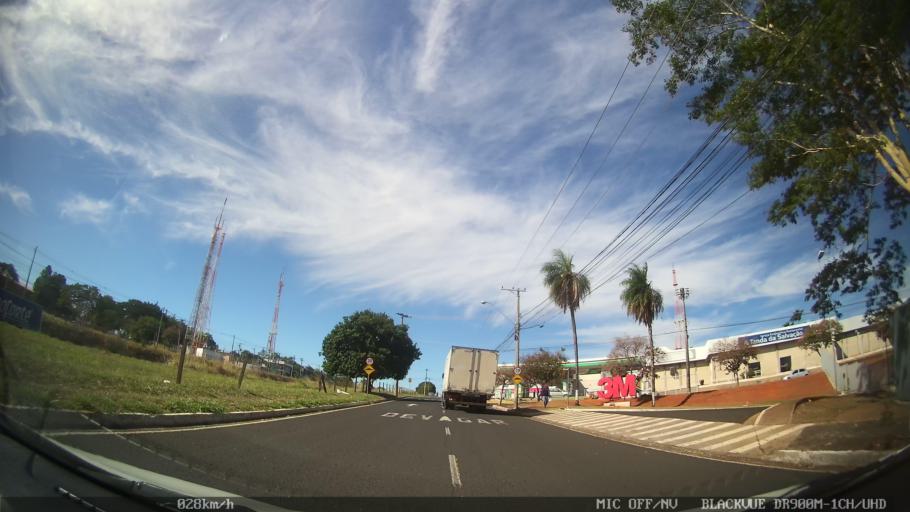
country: BR
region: Sao Paulo
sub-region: Sao Jose Do Rio Preto
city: Sao Jose do Rio Preto
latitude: -20.8021
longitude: -49.3498
